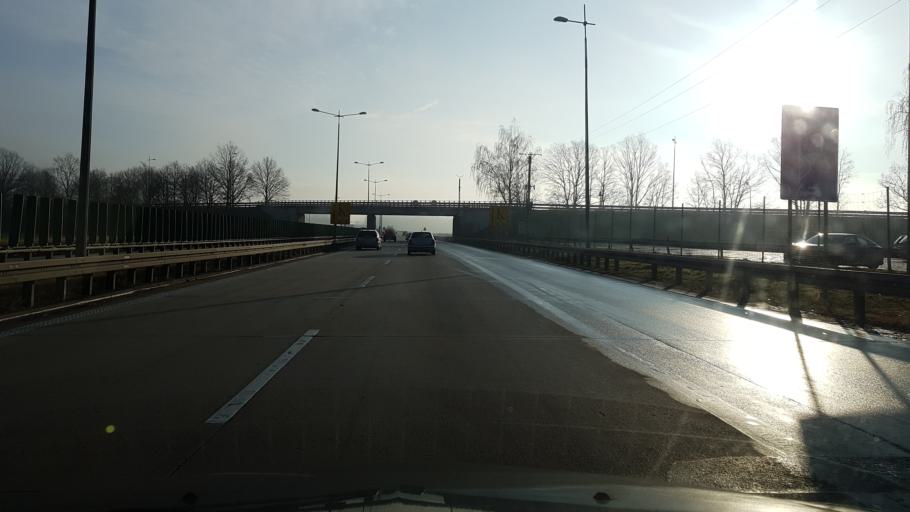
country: PL
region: Lower Silesian Voivodeship
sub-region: Powiat zlotoryjski
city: Olszanica
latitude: 51.2752
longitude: 15.7936
